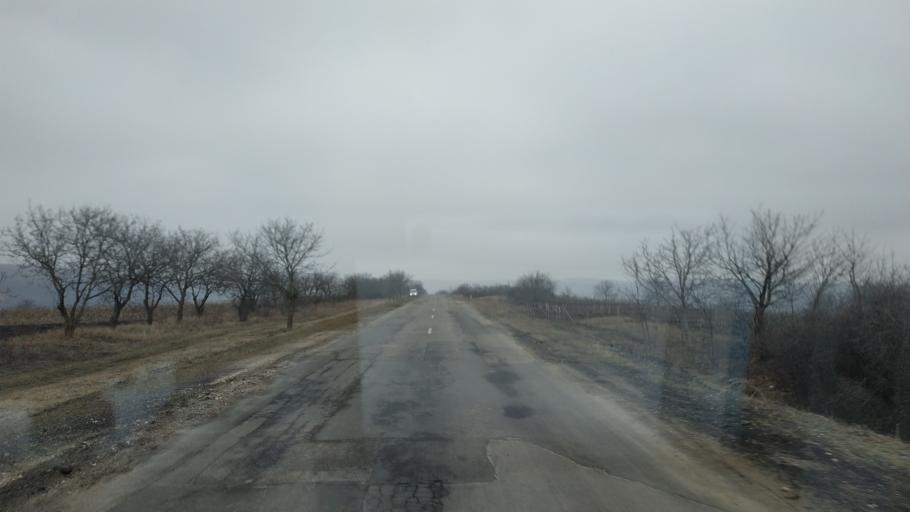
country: MD
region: Stinga Nistrului
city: Bucovat
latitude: 47.0184
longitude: 28.4290
